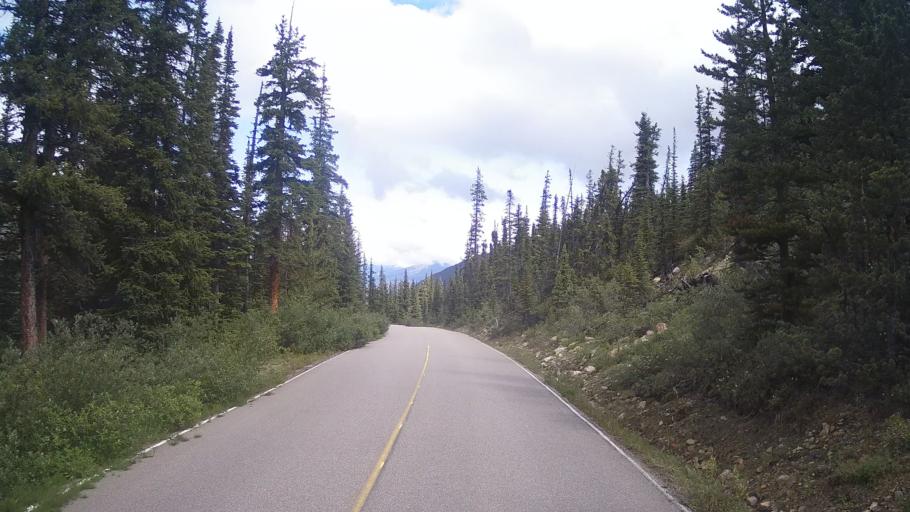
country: CA
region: Alberta
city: Jasper Park Lodge
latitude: 52.7056
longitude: -118.0588
